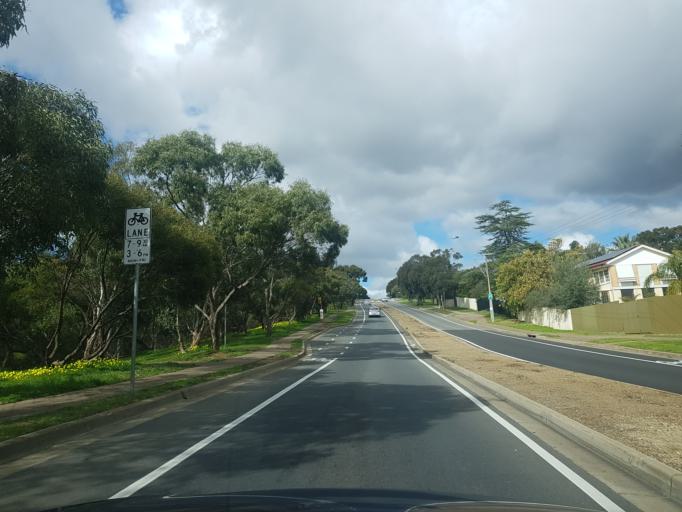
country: AU
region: South Australia
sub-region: Tea Tree Gully
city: Modbury
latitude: -34.8136
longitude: 138.6605
